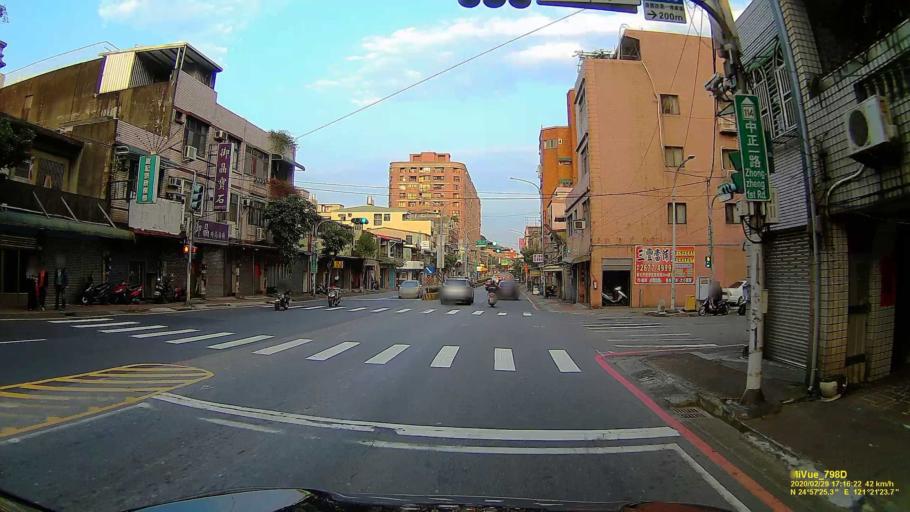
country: TW
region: Taiwan
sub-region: Taoyuan
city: Taoyuan
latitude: 24.9570
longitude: 121.3567
